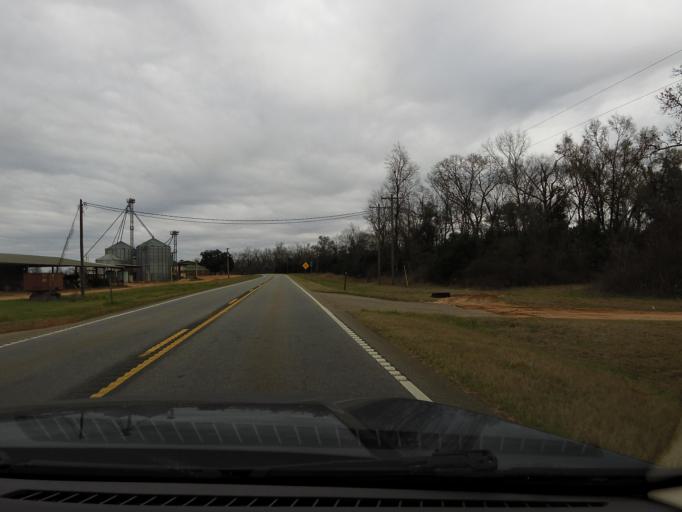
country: US
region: Georgia
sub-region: Randolph County
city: Shellman
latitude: 31.7741
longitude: -84.6881
